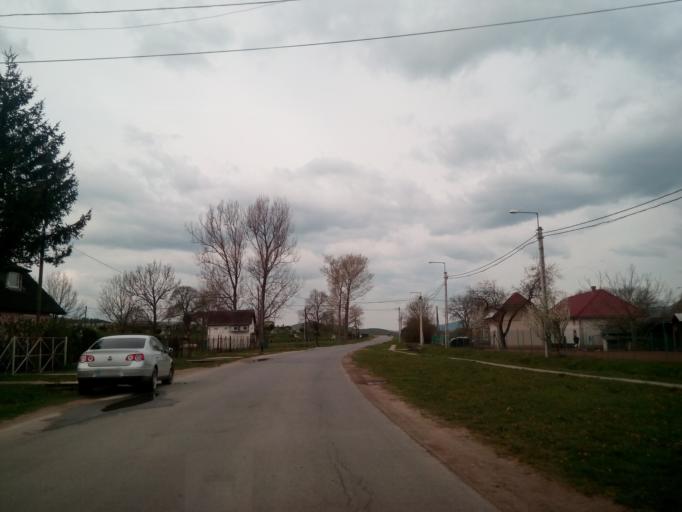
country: SK
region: Kosicky
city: Medzev
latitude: 48.5559
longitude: 20.8382
